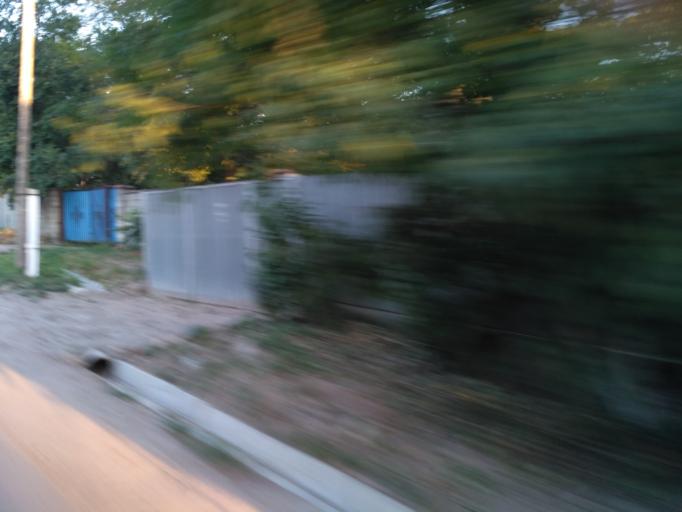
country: KZ
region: Almaty Qalasy
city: Almaty
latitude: 43.1741
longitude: 76.7647
